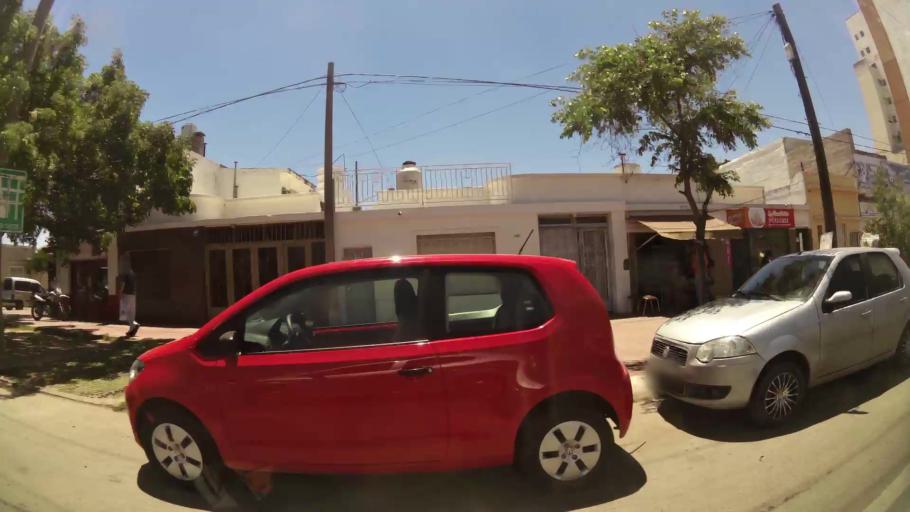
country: AR
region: Cordoba
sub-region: Departamento de Capital
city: Cordoba
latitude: -31.4341
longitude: -64.1321
